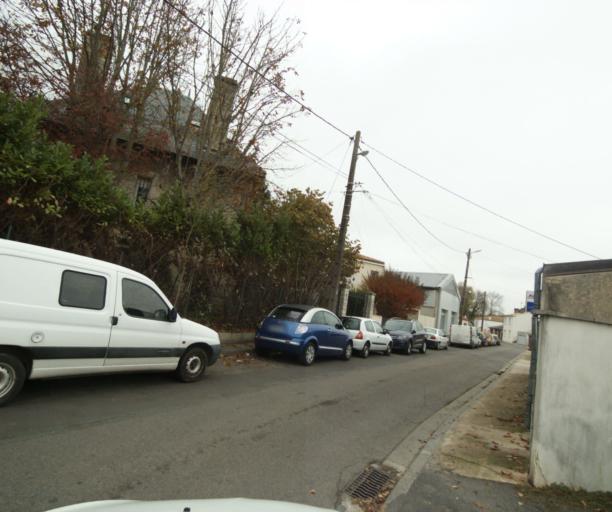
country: FR
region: Poitou-Charentes
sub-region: Departement de la Charente-Maritime
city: Saintes
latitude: 45.7473
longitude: -0.6238
